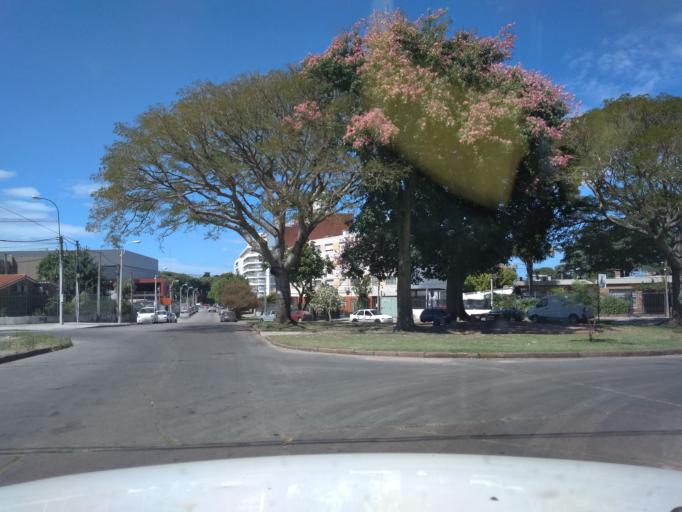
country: UY
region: Montevideo
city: Montevideo
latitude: -34.8888
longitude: -56.1204
